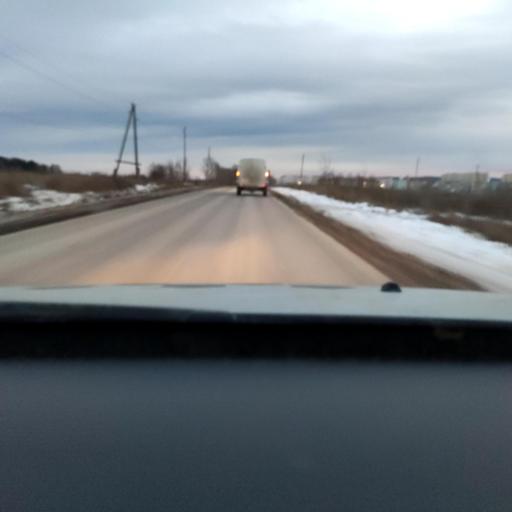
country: RU
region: Perm
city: Gamovo
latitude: 57.8788
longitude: 56.1017
